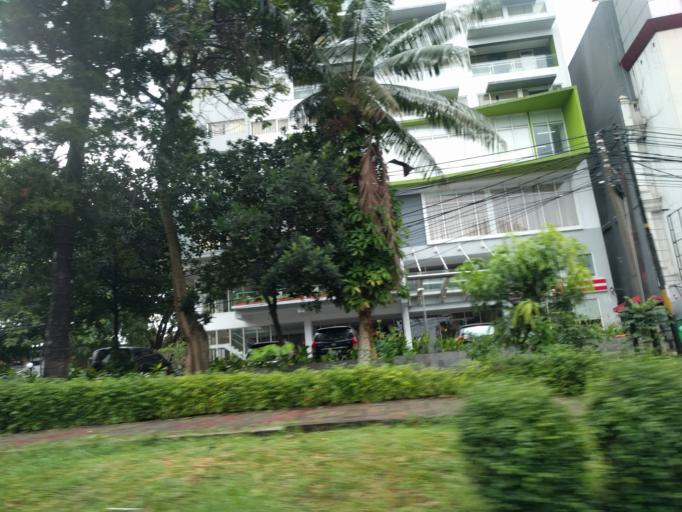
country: ID
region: West Java
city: Bogor
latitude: -6.5859
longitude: 106.8057
